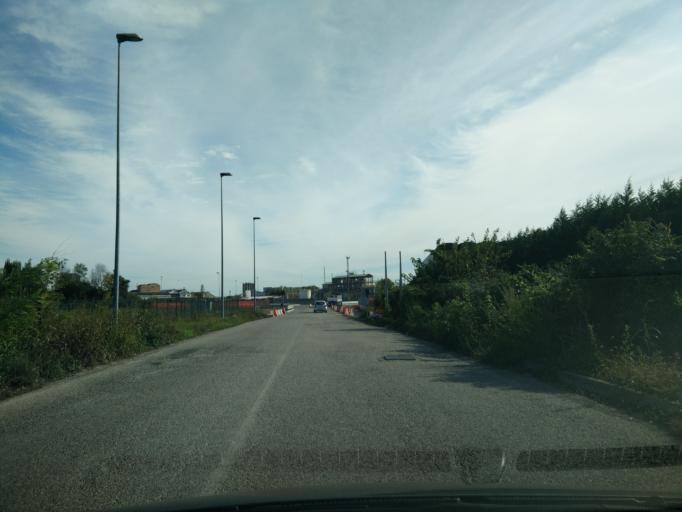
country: IT
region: Veneto
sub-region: Provincia di Venezia
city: Mestre
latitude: 45.4494
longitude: 12.2108
